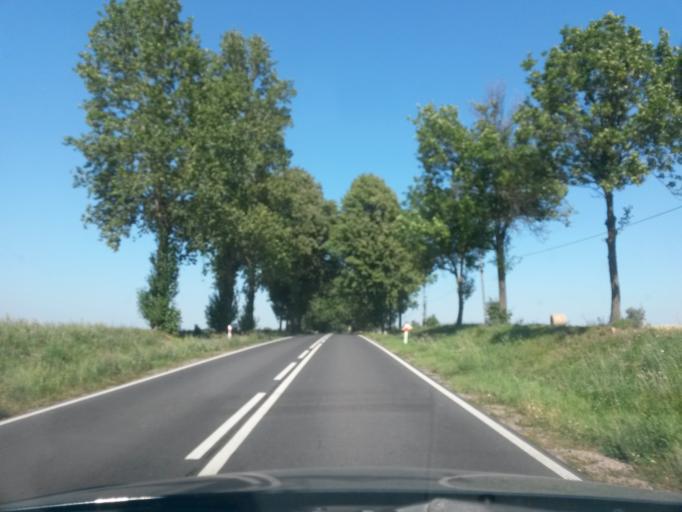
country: PL
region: Warmian-Masurian Voivodeship
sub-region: Powiat ilawski
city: Lubawa
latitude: 53.4042
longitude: 19.7992
